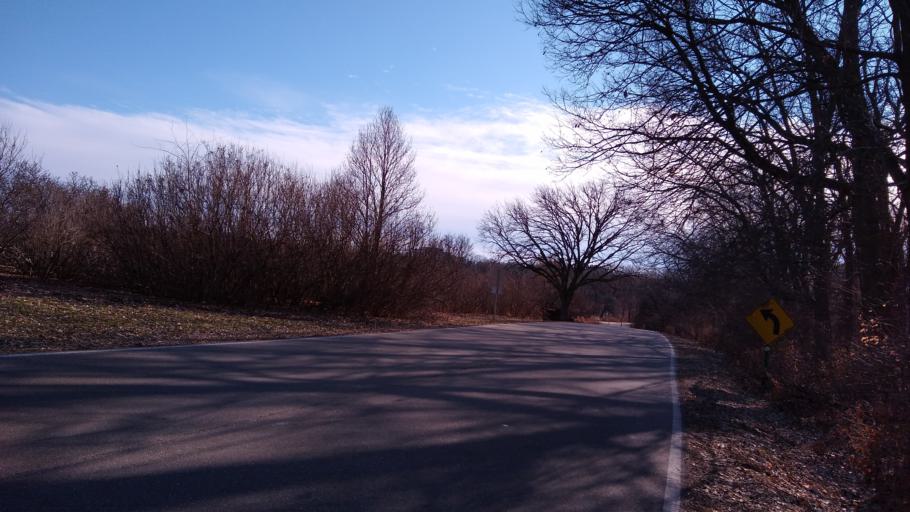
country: US
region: Wisconsin
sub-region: Dane County
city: Shorewood Hills
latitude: 43.0417
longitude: -89.4328
